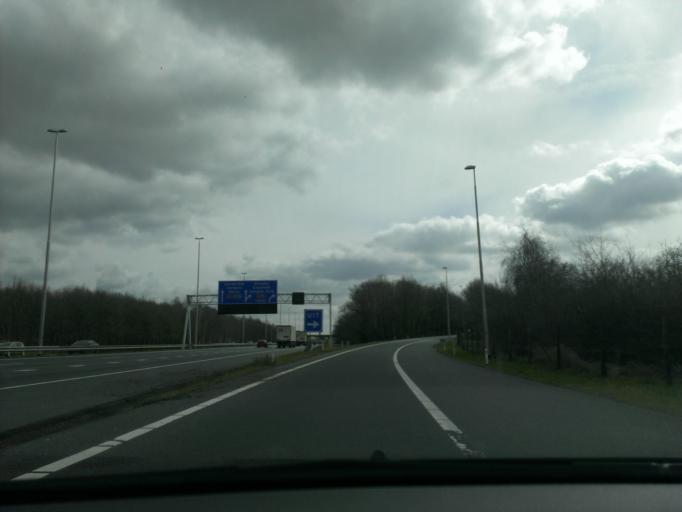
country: NL
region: Overijssel
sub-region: Gemeente Borne
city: Borne
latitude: 52.2954
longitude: 6.7253
